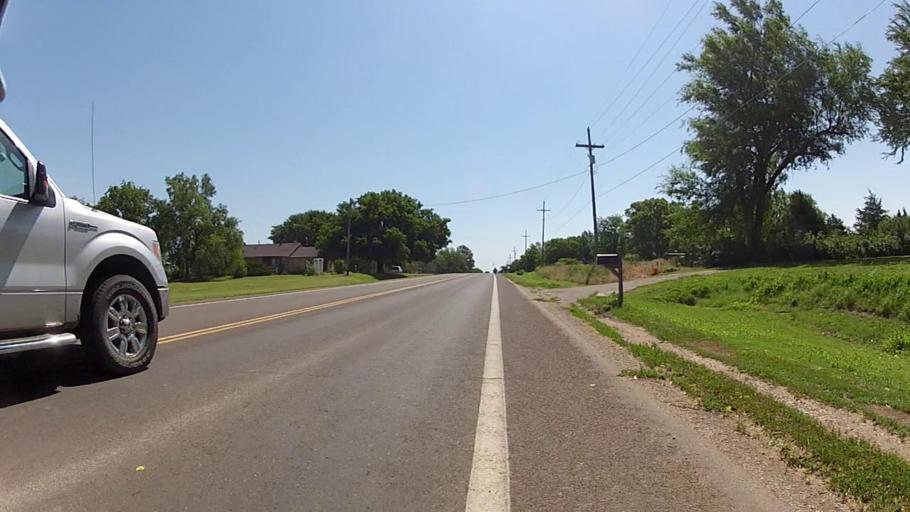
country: US
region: Kansas
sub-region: Sumner County
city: Caldwell
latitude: 37.0324
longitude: -97.5993
